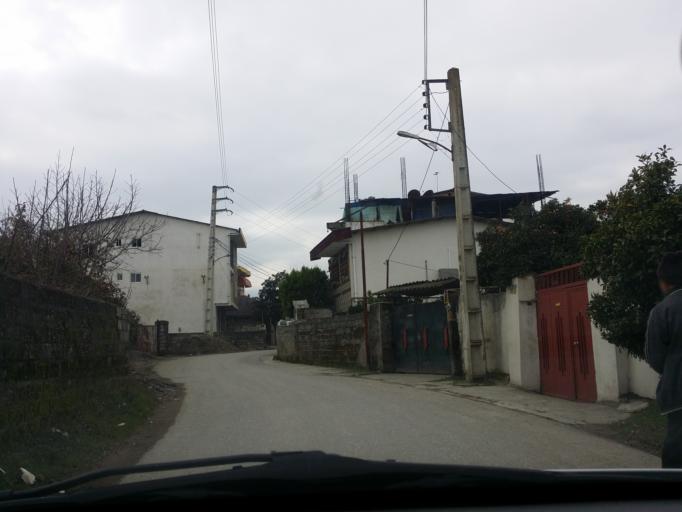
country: IR
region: Mazandaran
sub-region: Nowshahr
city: Nowshahr
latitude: 36.6473
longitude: 51.4762
